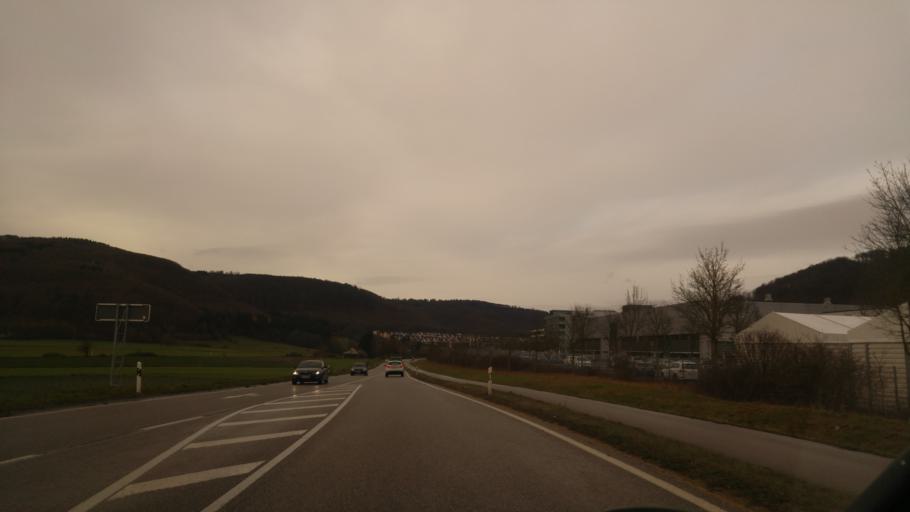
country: DE
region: Baden-Wuerttemberg
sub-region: Regierungsbezirk Stuttgart
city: Konigsbronn
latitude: 48.7622
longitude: 10.1031
